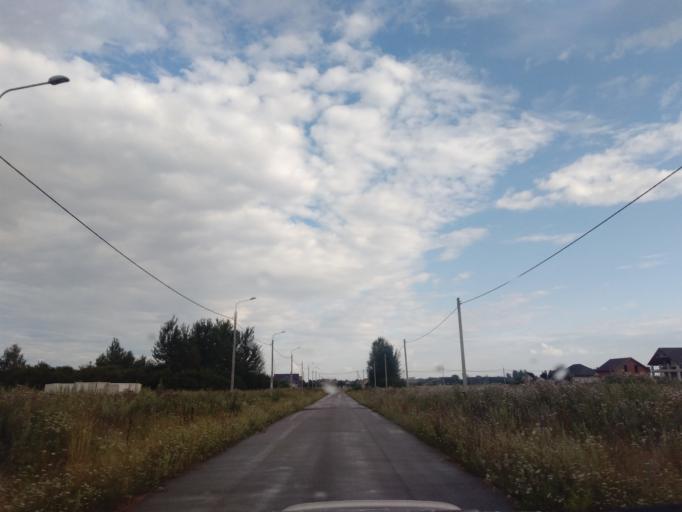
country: BY
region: Minsk
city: Kapyl'
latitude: 53.1653
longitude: 27.0785
